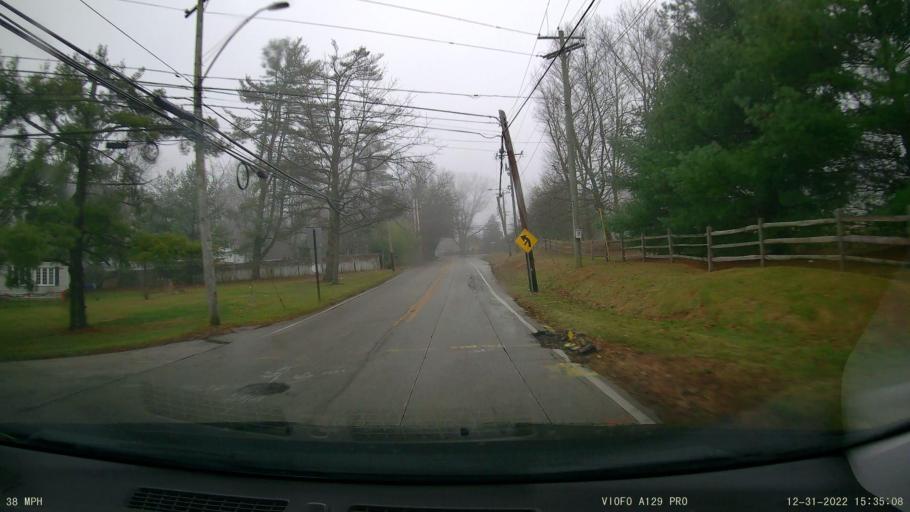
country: US
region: Pennsylvania
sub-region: Delaware County
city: Radnor
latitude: 40.0617
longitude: -75.3739
